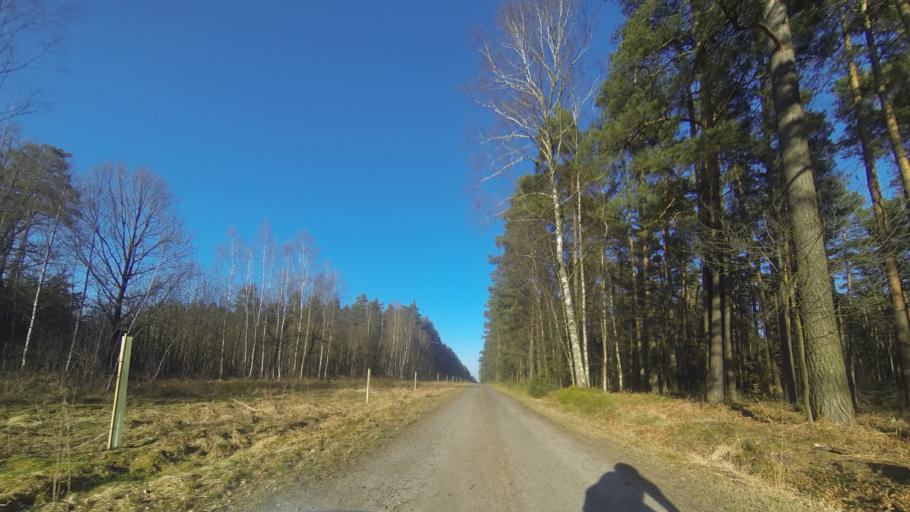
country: DE
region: Saxony
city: Tauscha
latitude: 51.2383
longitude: 13.8113
